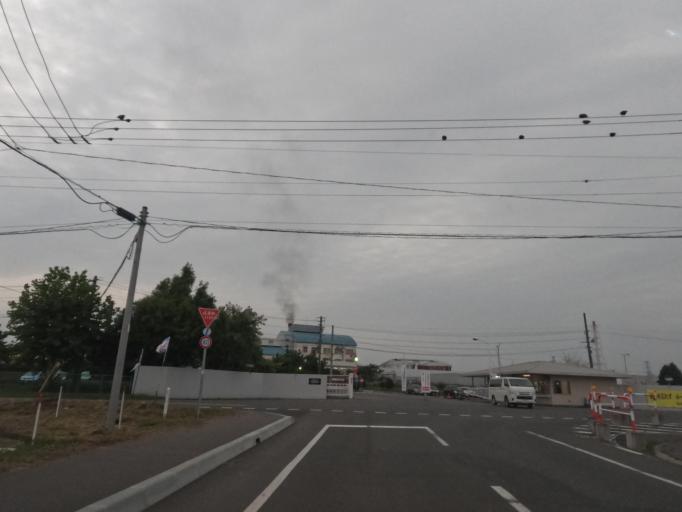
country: JP
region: Hokkaido
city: Date
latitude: 42.4779
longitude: 140.8443
